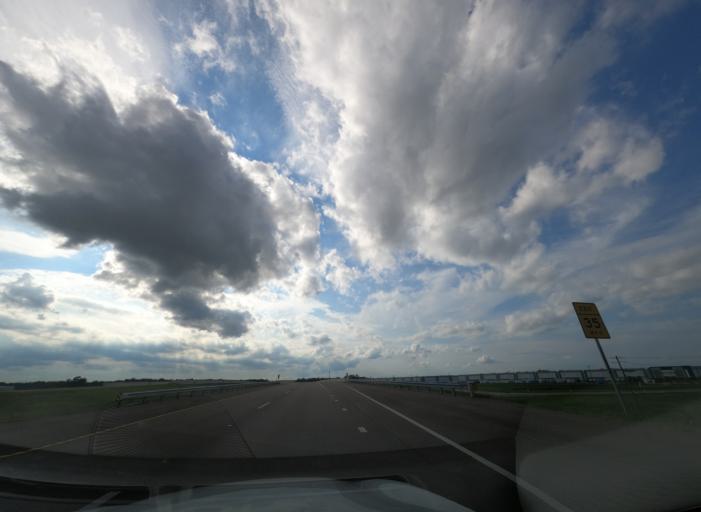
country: US
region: Tennessee
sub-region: Fayette County
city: Piperton
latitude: 34.9855
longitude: -89.5948
